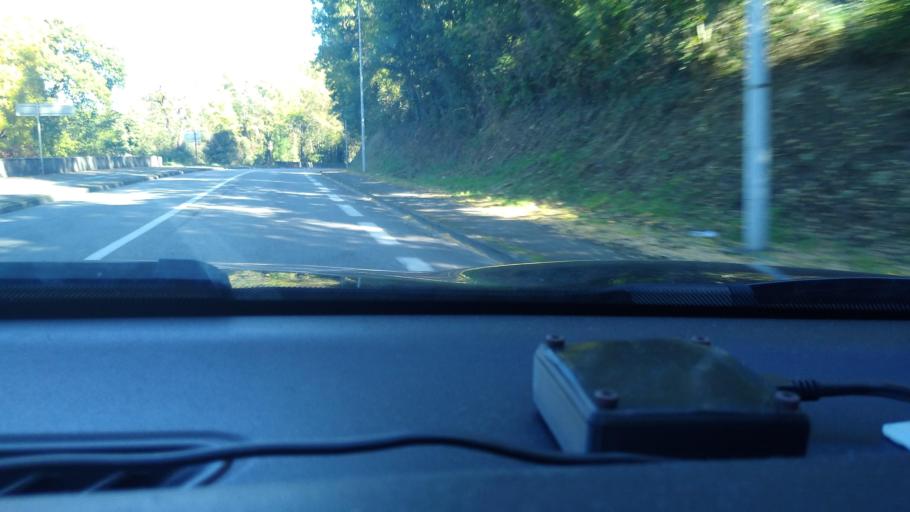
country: FR
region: Midi-Pyrenees
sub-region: Departement de l'Ariege
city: Foix
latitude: 42.9796
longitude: 1.6103
